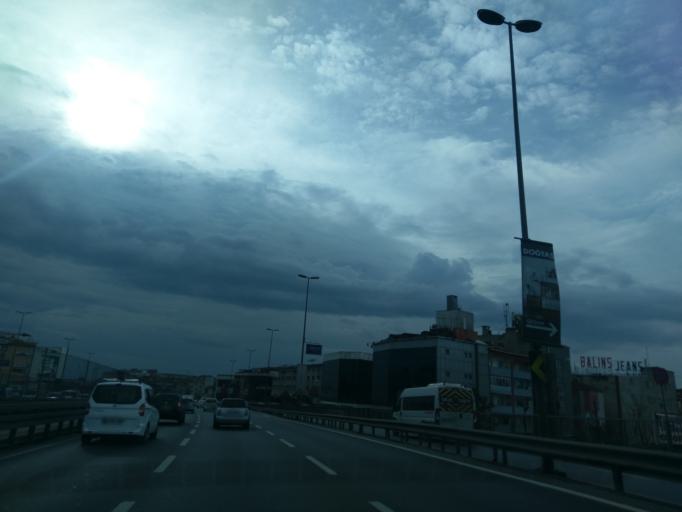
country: TR
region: Istanbul
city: Mahmutbey
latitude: 40.9975
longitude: 28.7968
